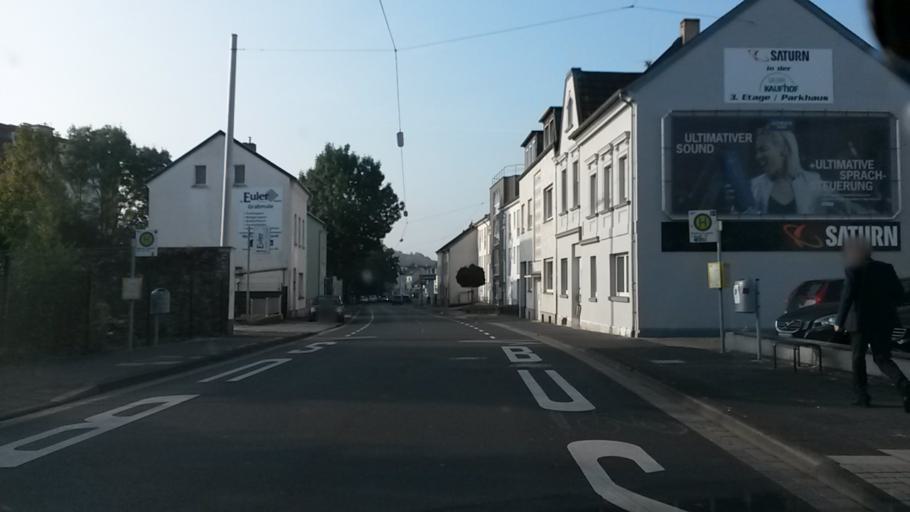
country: DE
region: North Rhine-Westphalia
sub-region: Regierungsbezirk Koln
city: Siegburg
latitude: 50.8055
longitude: 7.2089
